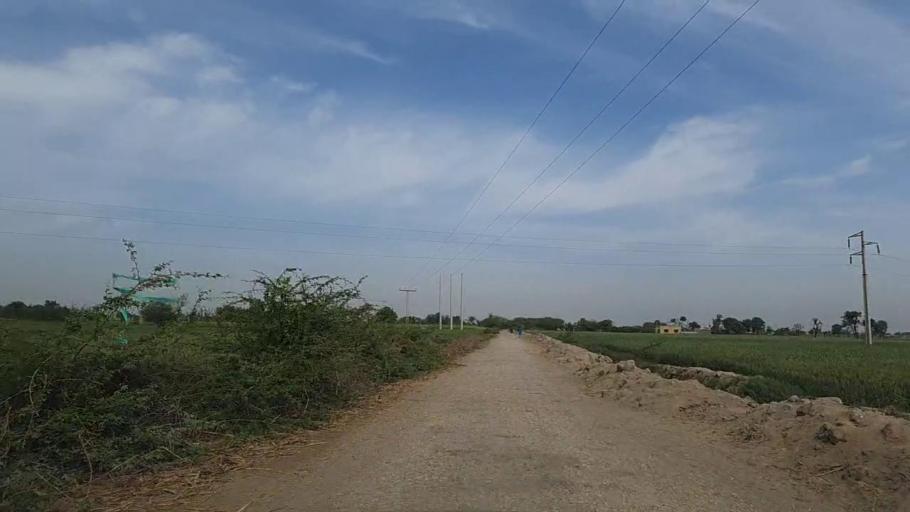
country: PK
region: Sindh
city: Samaro
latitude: 25.2968
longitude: 69.4239
